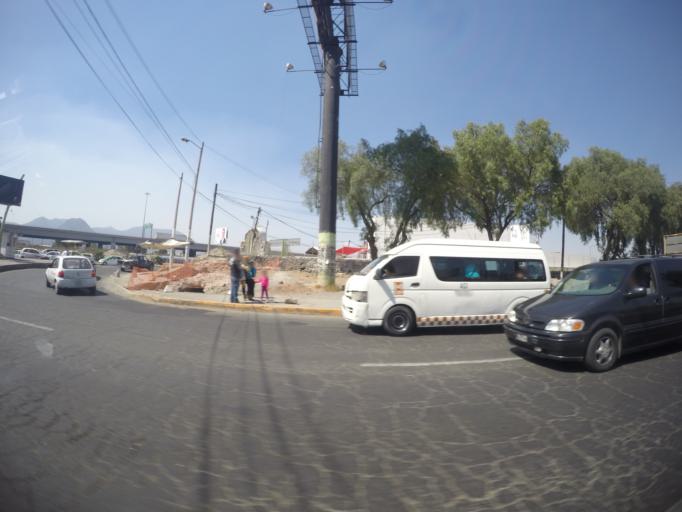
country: MX
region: Mexico
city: Ecatepec
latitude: 19.6022
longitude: -99.0341
